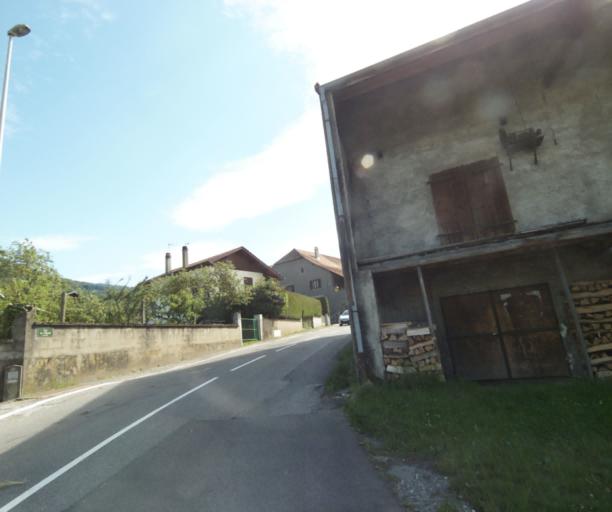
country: FR
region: Rhone-Alpes
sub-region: Departement de la Haute-Savoie
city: Perrignier
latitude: 46.2867
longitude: 6.4413
